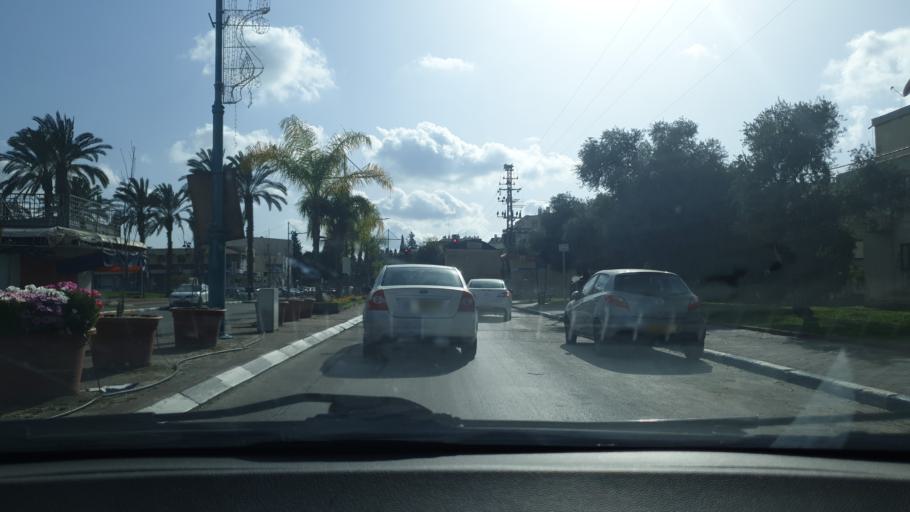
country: IL
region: Central District
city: Ramla
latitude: 31.9304
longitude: 34.8666
